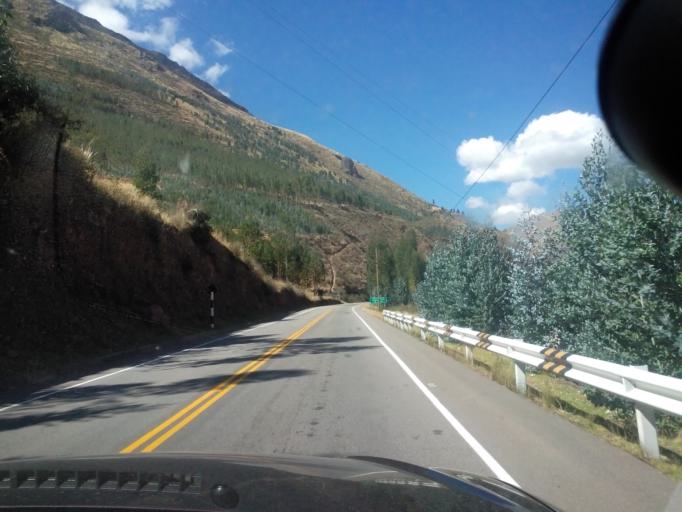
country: PE
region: Cusco
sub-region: Provincia de Quispicanchis
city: Cusipata
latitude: -13.9367
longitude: -71.5022
